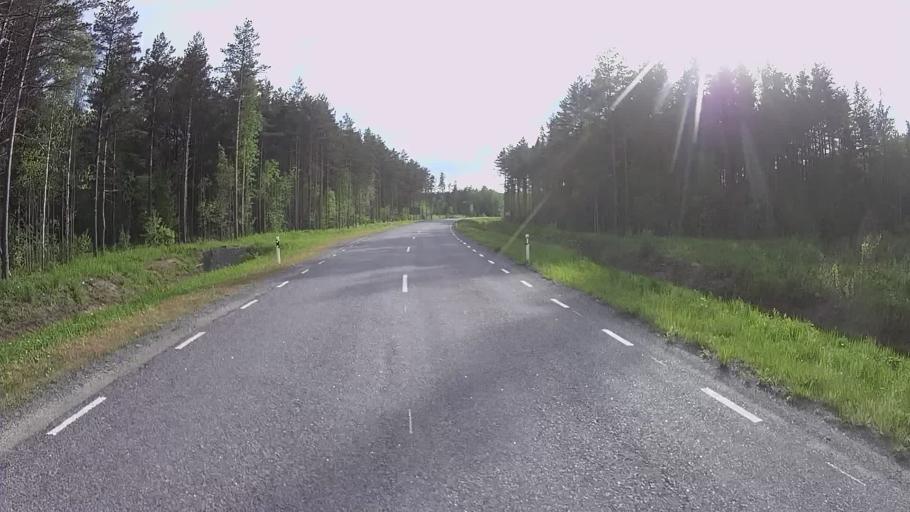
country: EE
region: Jogevamaa
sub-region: Mustvee linn
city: Mustvee
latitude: 59.0243
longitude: 27.0799
